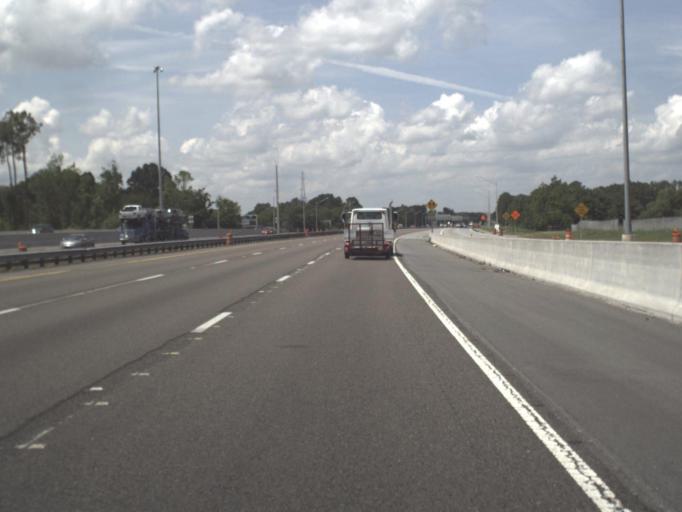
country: US
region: Florida
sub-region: Clay County
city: Bellair-Meadowbrook Terrace
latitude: 30.2094
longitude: -81.7589
